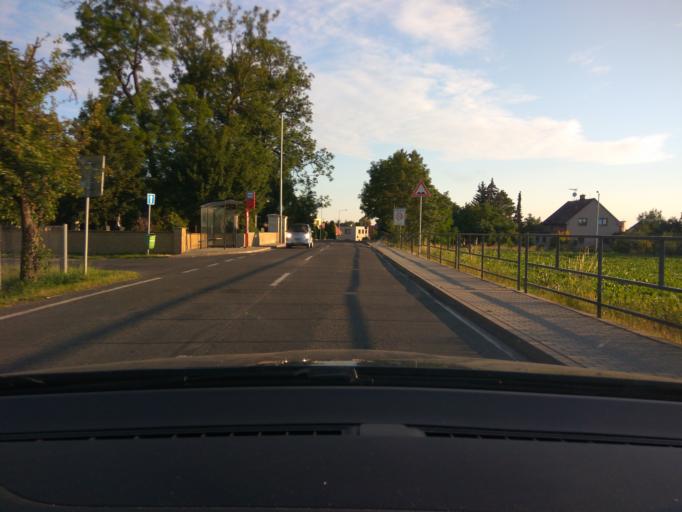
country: CZ
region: Central Bohemia
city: Hovorcovice
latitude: 50.1593
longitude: 14.5259
